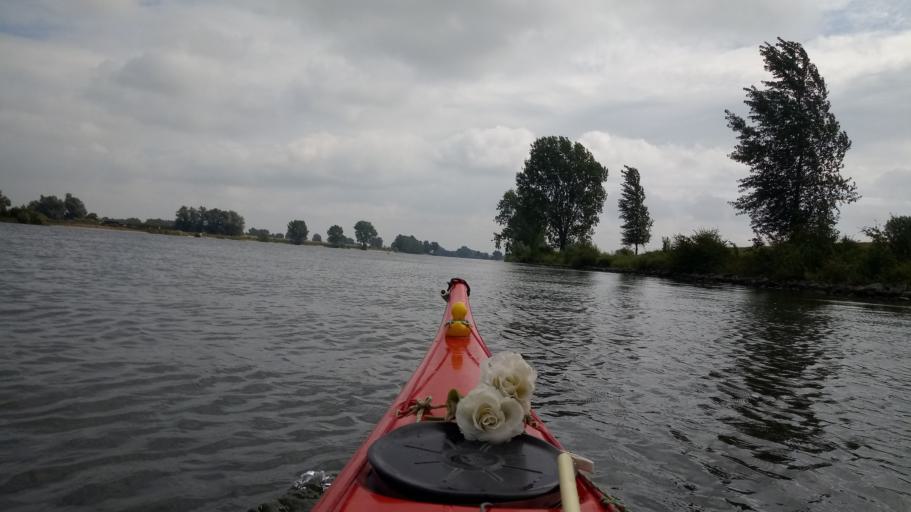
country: NL
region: Gelderland
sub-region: Gemeente Zaltbommel
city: Nederhemert-Noord
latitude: 51.7423
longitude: 5.1784
